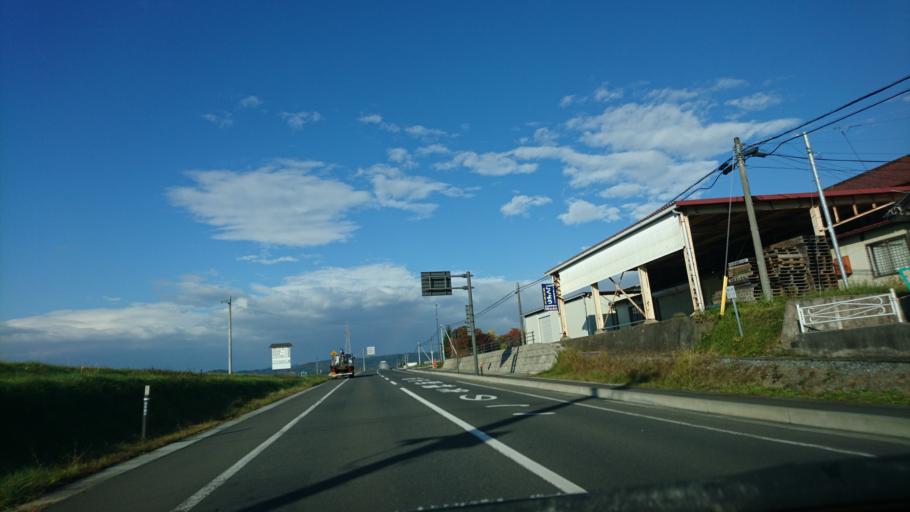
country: JP
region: Iwate
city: Ichinoseki
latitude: 39.0152
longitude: 141.1097
